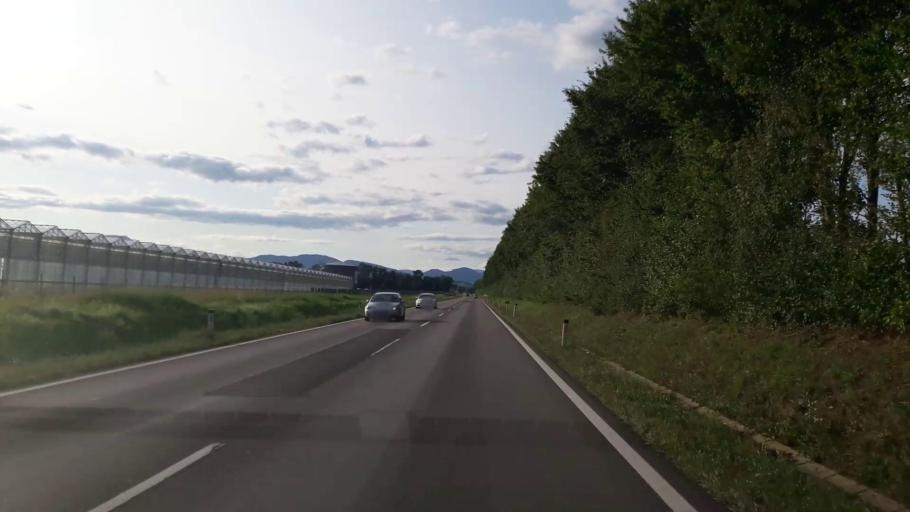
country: AT
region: Styria
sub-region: Politischer Bezirk Weiz
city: Gleisdorf
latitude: 47.1293
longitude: 15.6884
